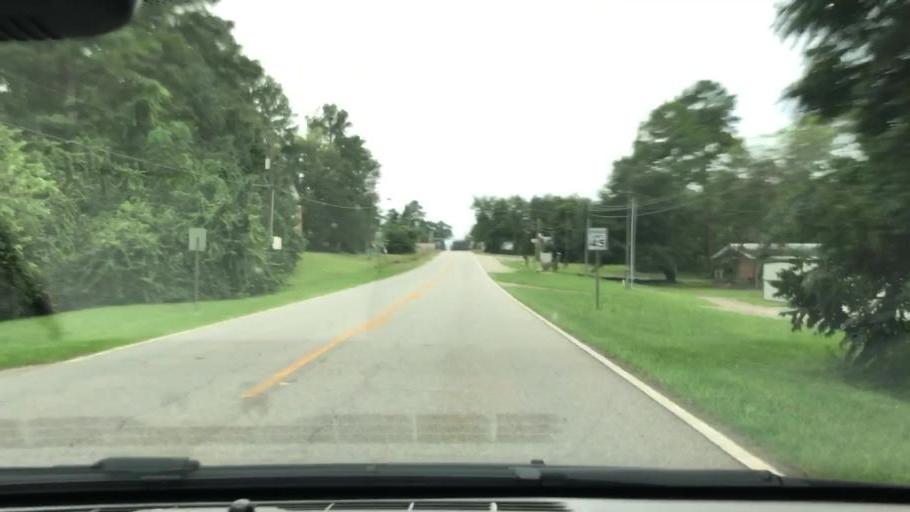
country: US
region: Georgia
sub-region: Early County
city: Blakely
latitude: 31.3951
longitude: -84.9329
